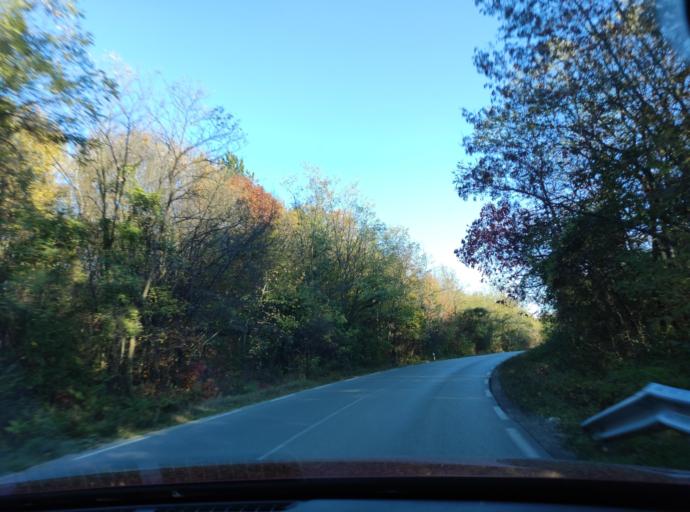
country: BG
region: Montana
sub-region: Obshtina Montana
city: Montana
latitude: 43.4012
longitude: 23.0905
